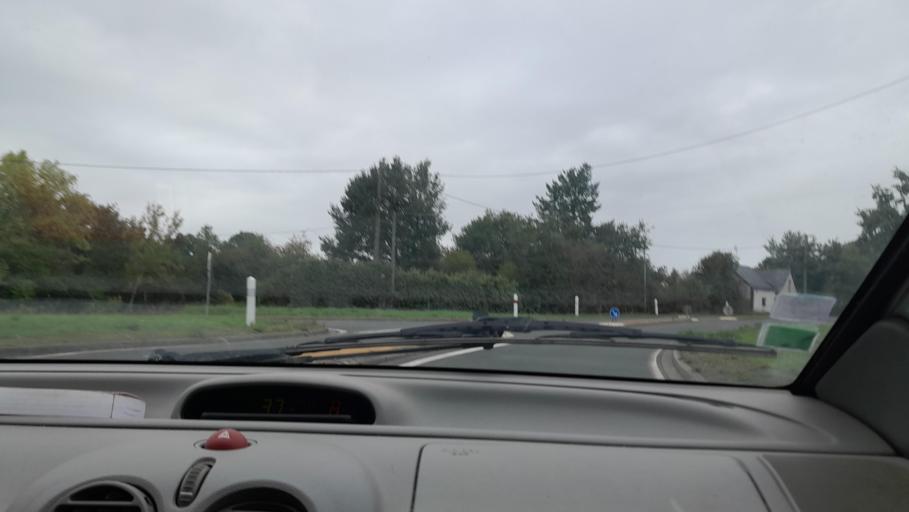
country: FR
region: Pays de la Loire
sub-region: Departement de la Loire-Atlantique
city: Saint-Mars-la-Jaille
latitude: 47.4712
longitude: -1.1749
